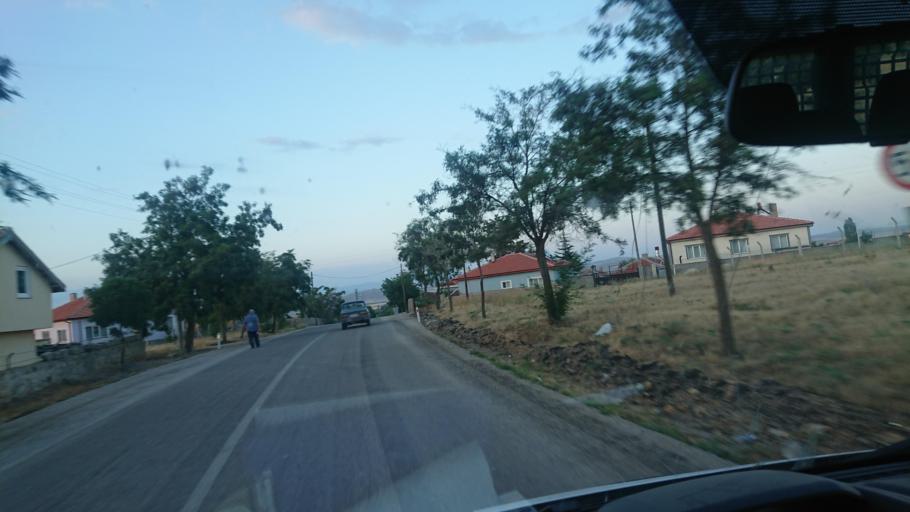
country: TR
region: Aksaray
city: Sariyahsi
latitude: 38.9770
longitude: 33.8371
